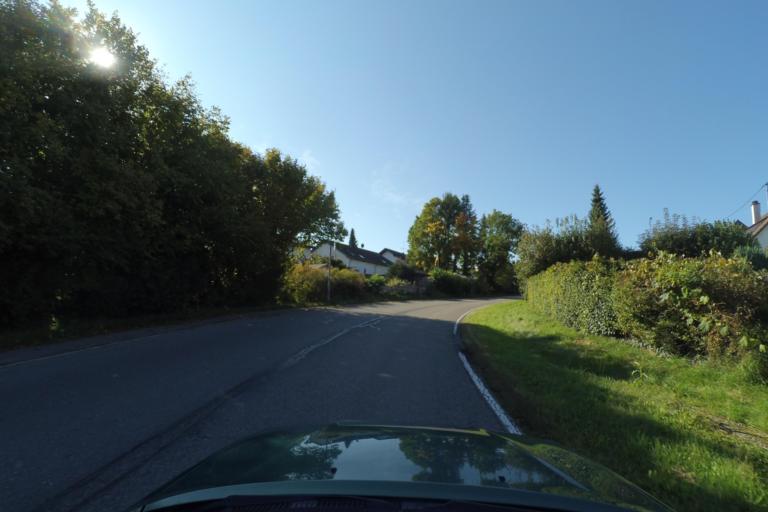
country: DE
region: Baden-Wuerttemberg
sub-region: Karlsruhe Region
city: Neuhausen
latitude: 48.8148
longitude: 8.7937
